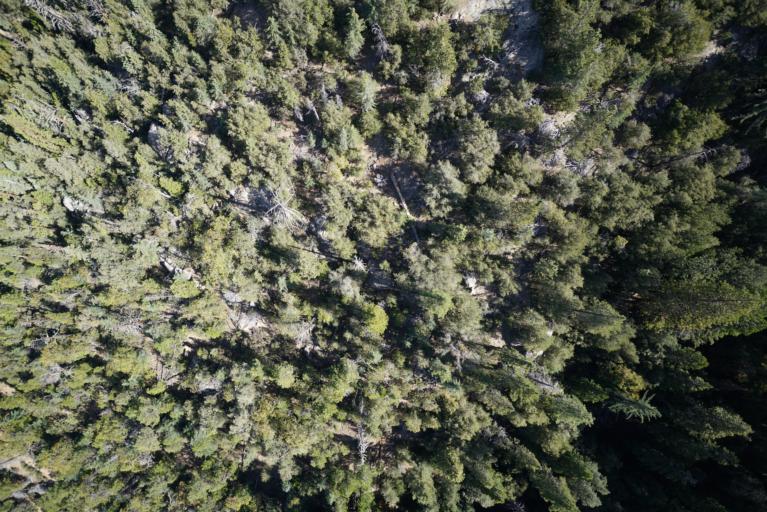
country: US
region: California
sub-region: Riverside County
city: Idyllwild
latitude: 33.7508
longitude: -116.6921
